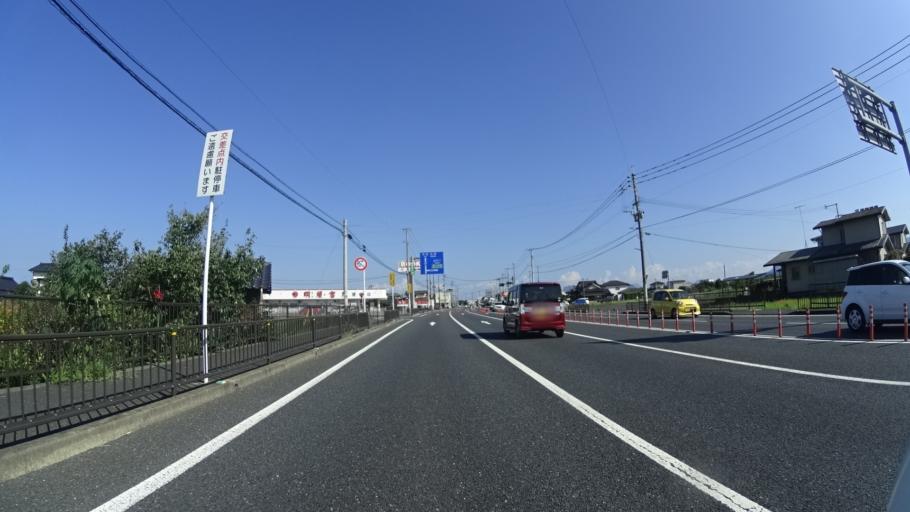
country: JP
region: Fukuoka
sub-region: Buzen-shi
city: Buzen
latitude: 33.6003
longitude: 131.1300
